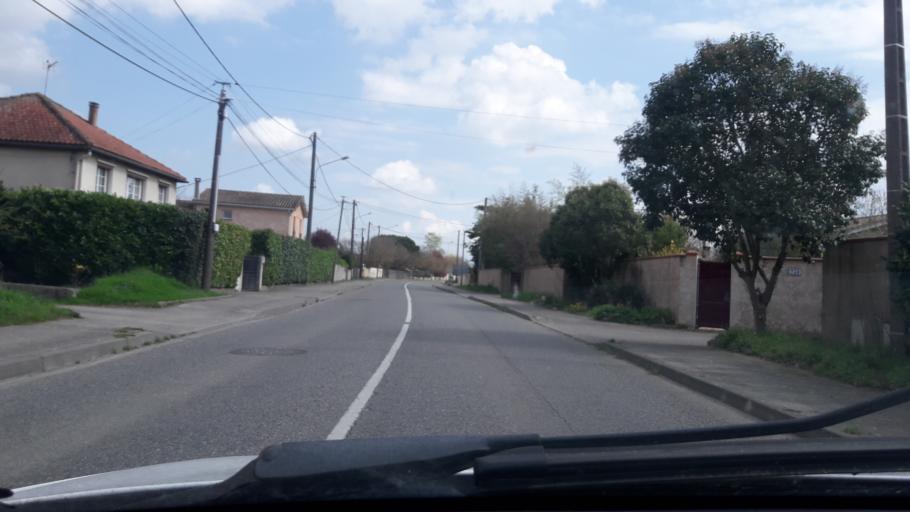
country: FR
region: Midi-Pyrenees
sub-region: Departement de la Haute-Garonne
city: Seysses
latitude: 43.4967
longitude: 1.3010
